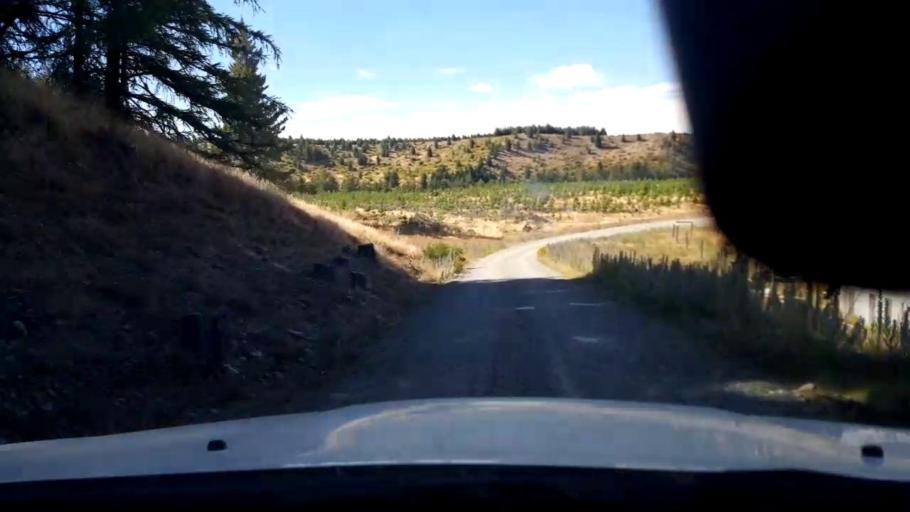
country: NZ
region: Canterbury
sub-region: Timaru District
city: Pleasant Point
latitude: -44.0130
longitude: 170.4731
